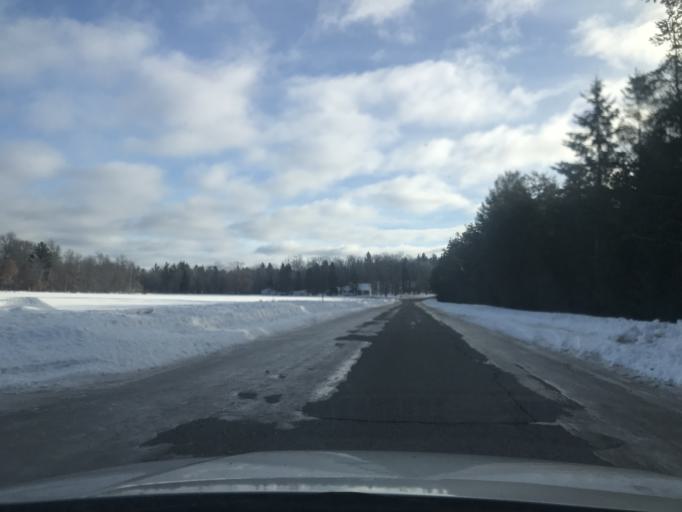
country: US
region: Wisconsin
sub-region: Marinette County
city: Niagara
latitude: 45.6262
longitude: -87.9706
